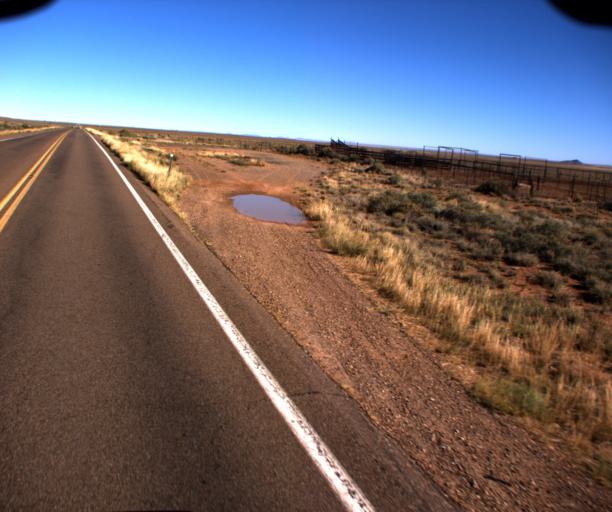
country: US
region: Arizona
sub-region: Navajo County
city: Snowflake
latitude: 34.7091
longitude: -110.1110
